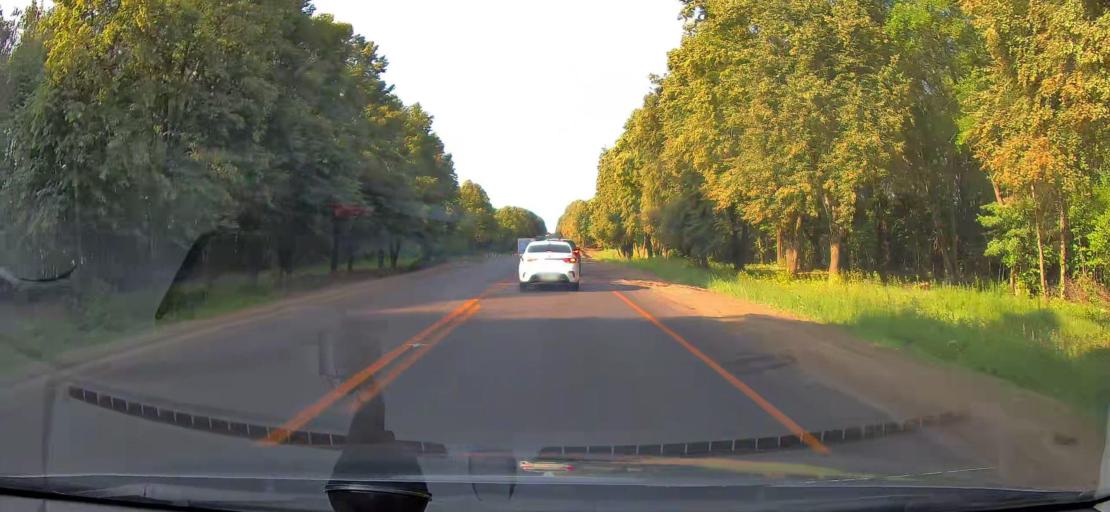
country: RU
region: Orjol
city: Spasskoye-Lutovinovo
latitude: 53.3683
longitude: 36.7304
